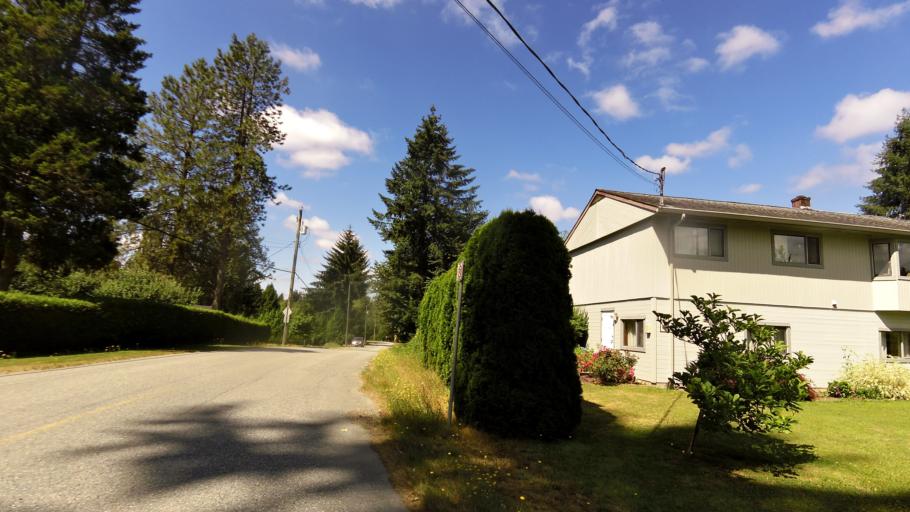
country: CA
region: British Columbia
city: Maple Ridge
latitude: 49.2157
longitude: -122.5238
